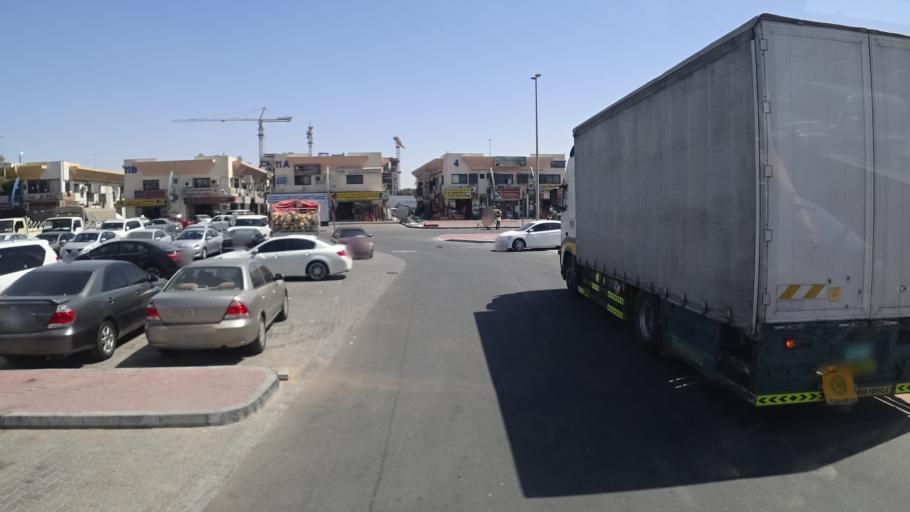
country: AE
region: Ash Shariqah
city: Sharjah
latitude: 25.1739
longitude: 55.3934
